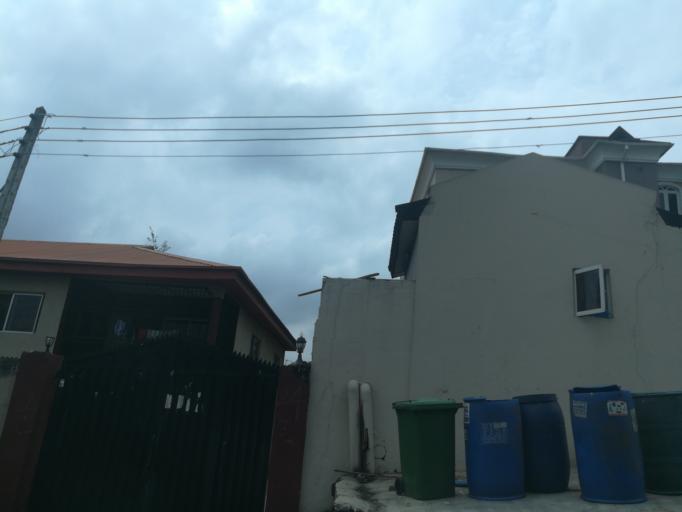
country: NG
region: Lagos
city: Ojota
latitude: 6.5908
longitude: 3.3645
